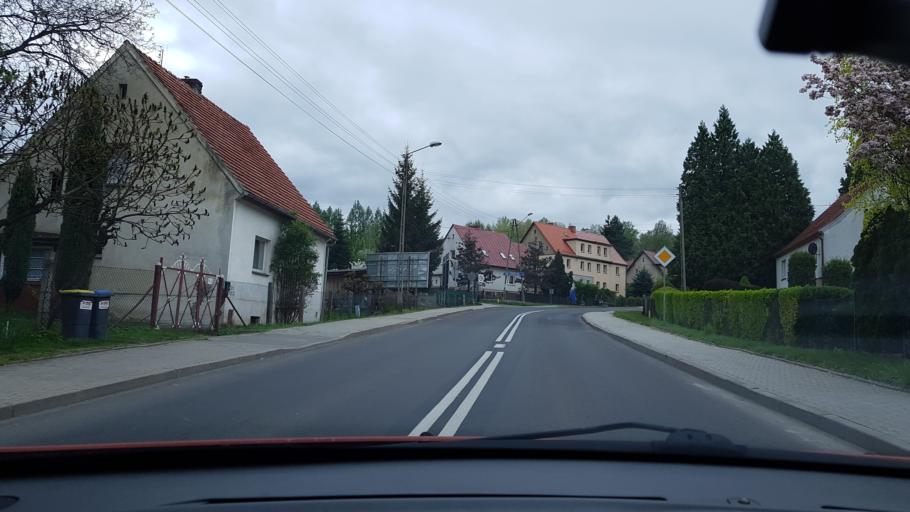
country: PL
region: Opole Voivodeship
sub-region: Powiat nyski
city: Glucholazy
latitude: 50.3171
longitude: 17.3649
